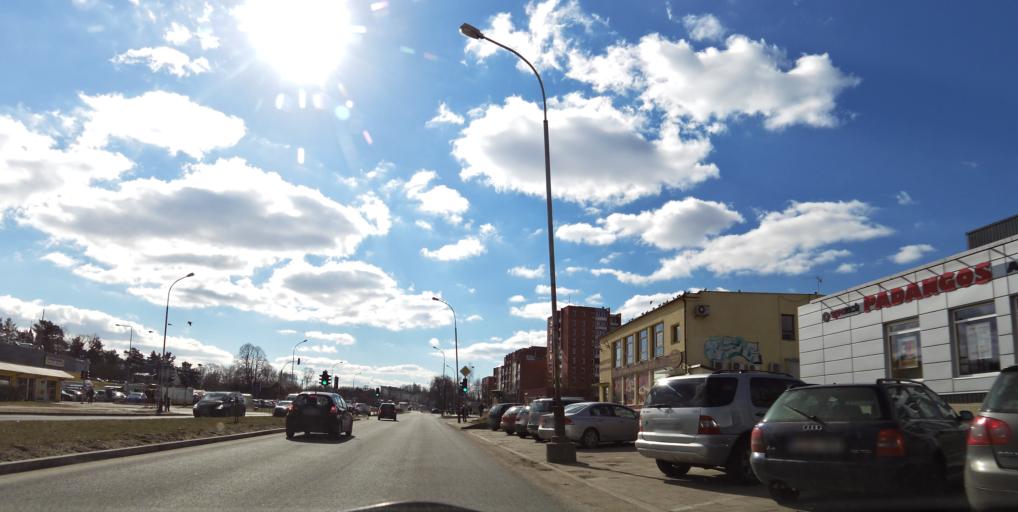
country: LT
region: Vilnius County
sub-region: Vilnius
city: Fabijoniskes
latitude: 54.7441
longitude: 25.2775
